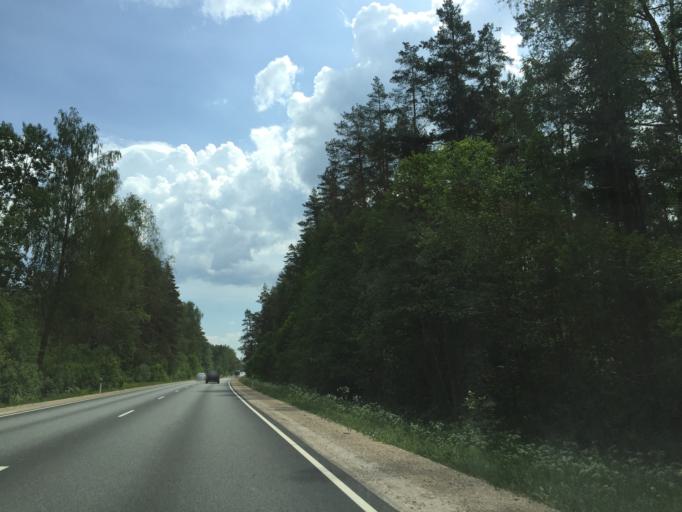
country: LV
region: Ikskile
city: Ikskile
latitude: 56.8899
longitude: 24.4795
